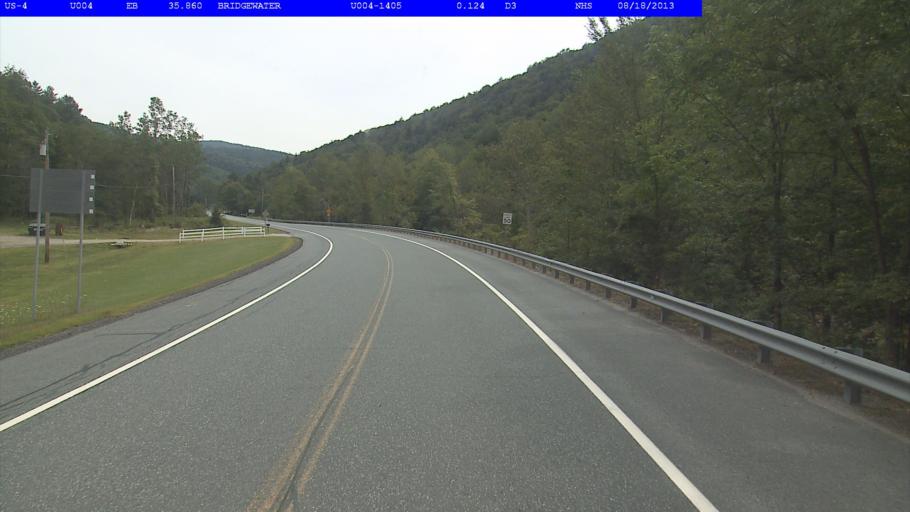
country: US
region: Vermont
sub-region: Rutland County
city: Rutland
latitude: 43.5998
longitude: -72.7474
